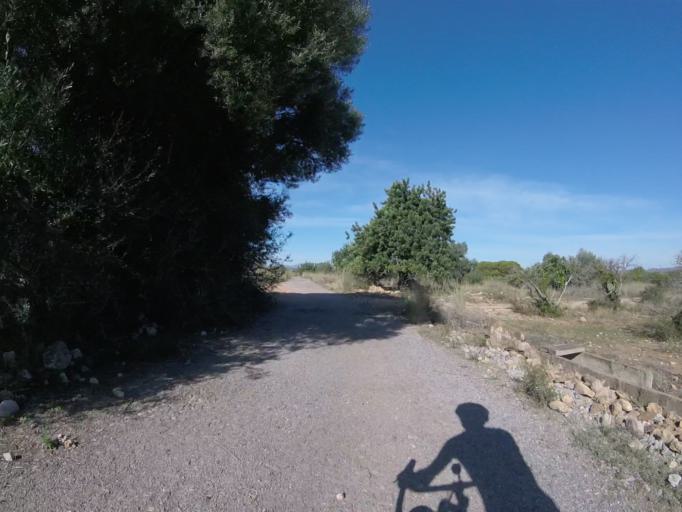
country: ES
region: Valencia
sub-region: Provincia de Castello
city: Torreblanca
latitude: 40.2076
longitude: 0.2459
